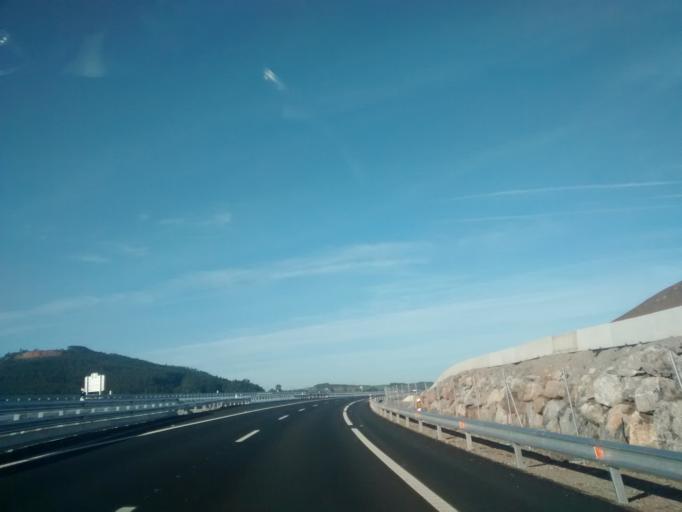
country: ES
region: Cantabria
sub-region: Provincia de Cantabria
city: Puente Viesgo
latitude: 43.3116
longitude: -3.9427
